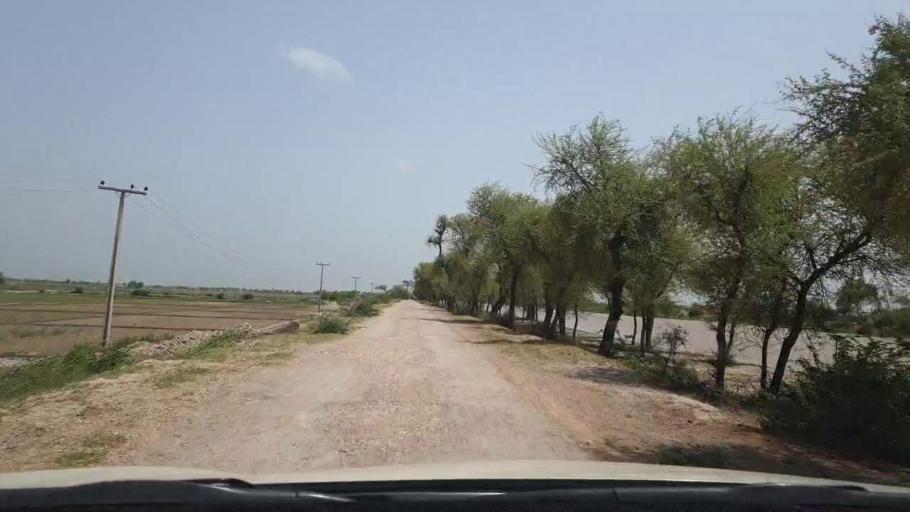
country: PK
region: Sindh
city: Talhar
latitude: 24.9077
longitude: 68.8376
